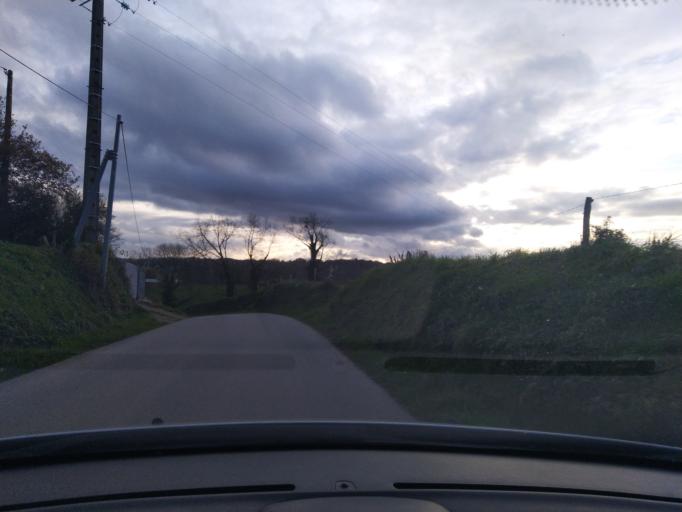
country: FR
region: Brittany
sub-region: Departement du Finistere
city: Guerlesquin
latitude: 48.5611
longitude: -3.6173
